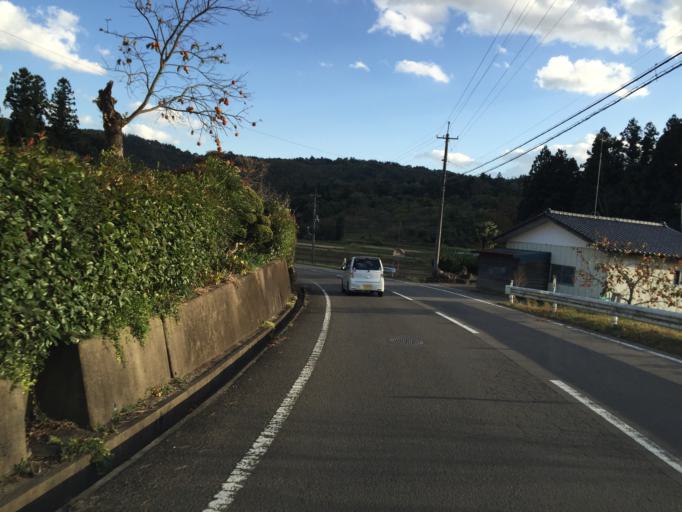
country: JP
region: Fukushima
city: Fukushima-shi
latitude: 37.7034
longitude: 140.4204
